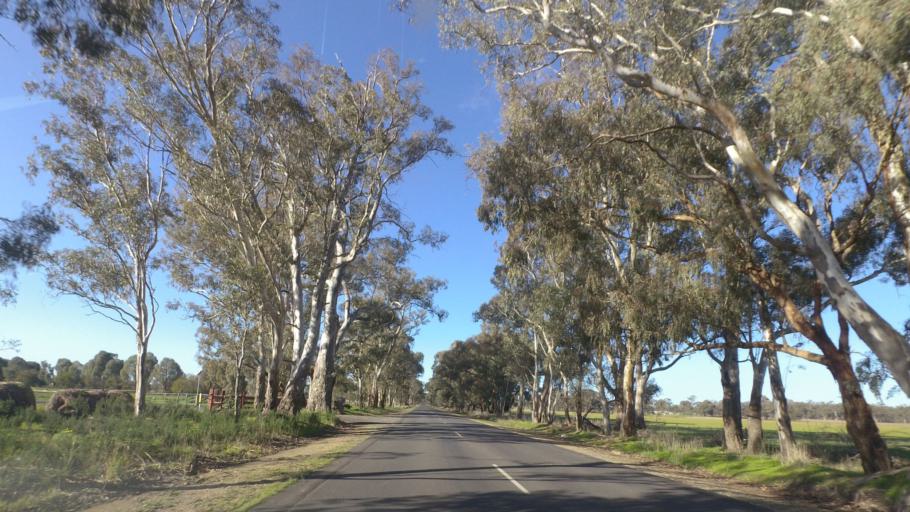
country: AU
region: Victoria
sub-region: Greater Bendigo
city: Epsom
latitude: -36.6607
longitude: 144.4631
